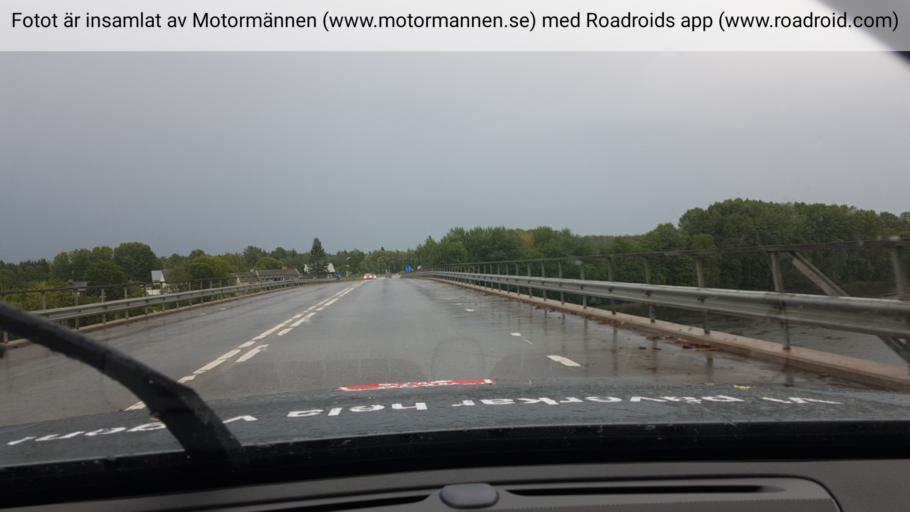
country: SE
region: Uppsala
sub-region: Alvkarleby Kommun
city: AElvkarleby
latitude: 60.6032
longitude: 17.4483
